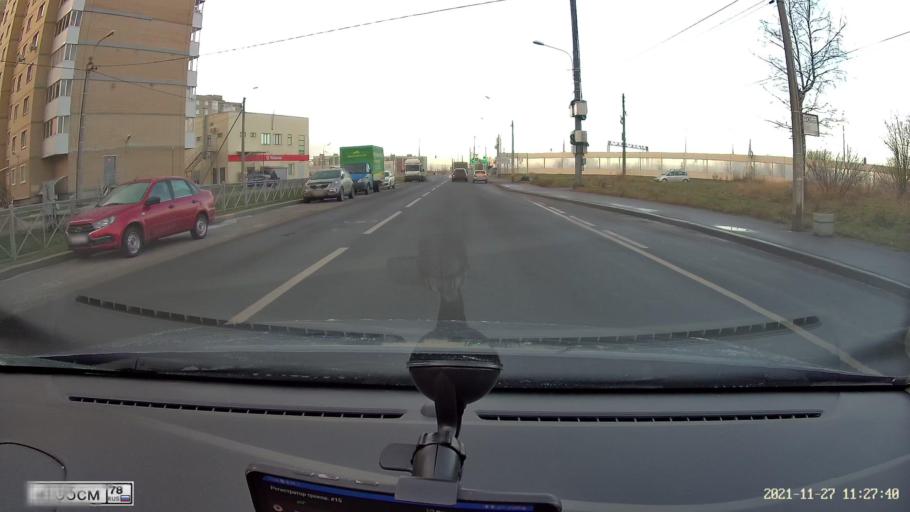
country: RU
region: St.-Petersburg
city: Krasnoye Selo
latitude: 59.7476
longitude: 30.0825
